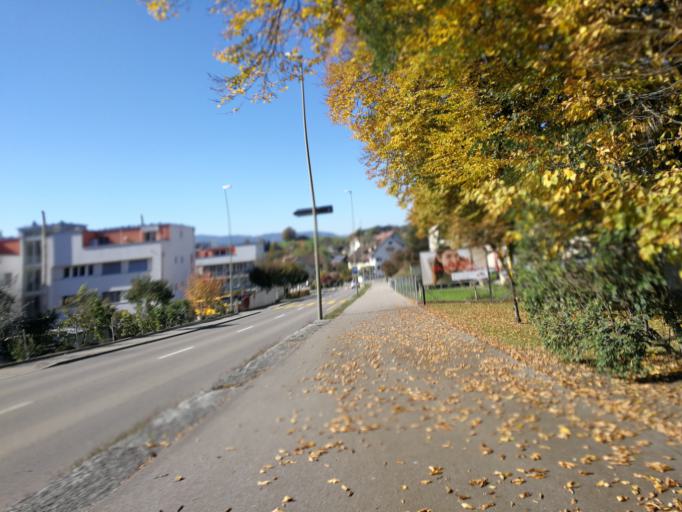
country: CH
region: Zurich
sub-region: Bezirk Hinwil
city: Gossau
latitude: 47.3073
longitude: 8.7623
